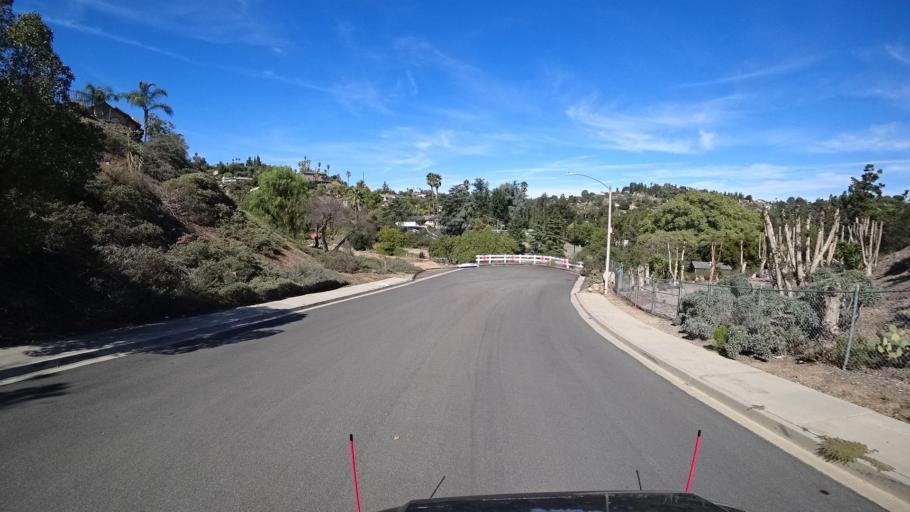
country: US
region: California
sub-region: San Diego County
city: Casa de Oro-Mount Helix
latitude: 32.7582
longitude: -116.9508
